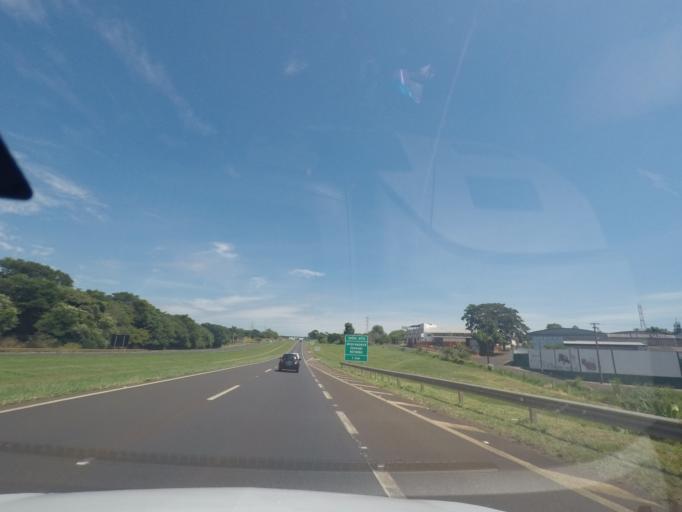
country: BR
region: Sao Paulo
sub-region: Araraquara
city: Araraquara
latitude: -21.8137
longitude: -48.1848
